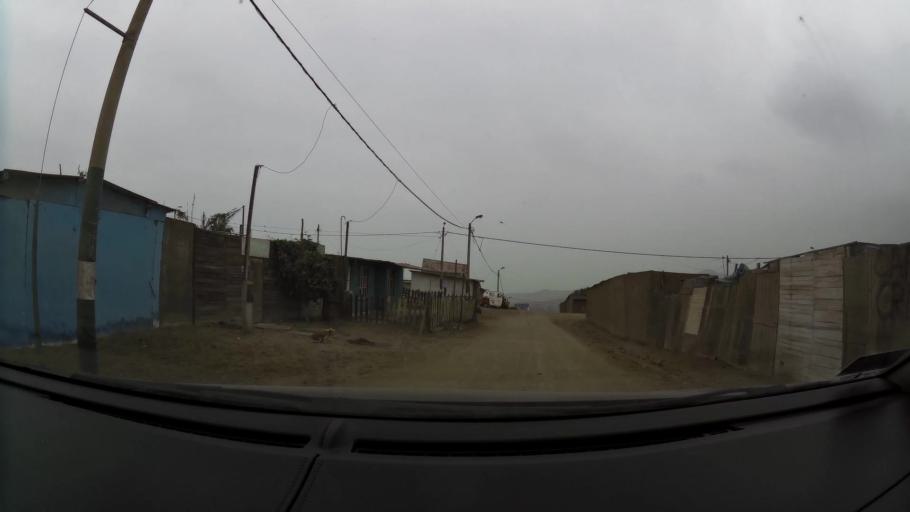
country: PE
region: Lima
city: Ventanilla
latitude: -11.8476
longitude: -77.1418
